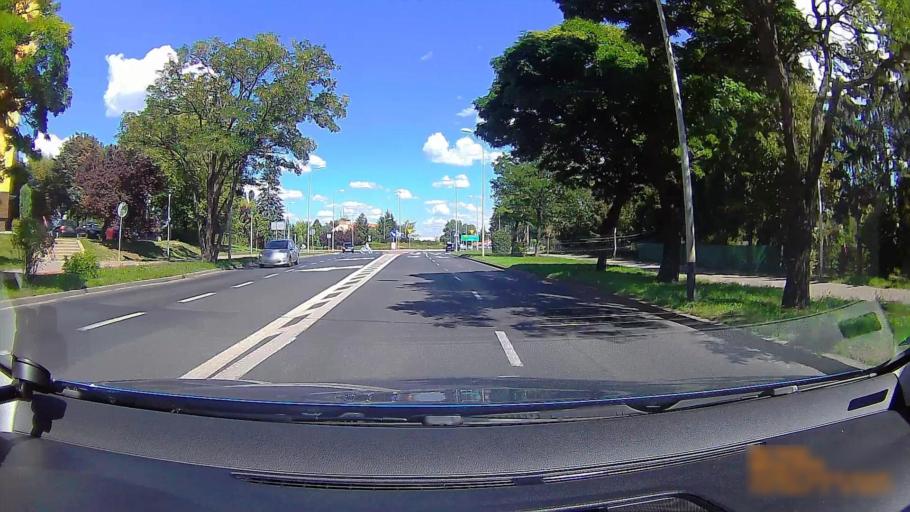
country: PL
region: Greater Poland Voivodeship
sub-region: Konin
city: Konin
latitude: 52.2288
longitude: 18.2795
